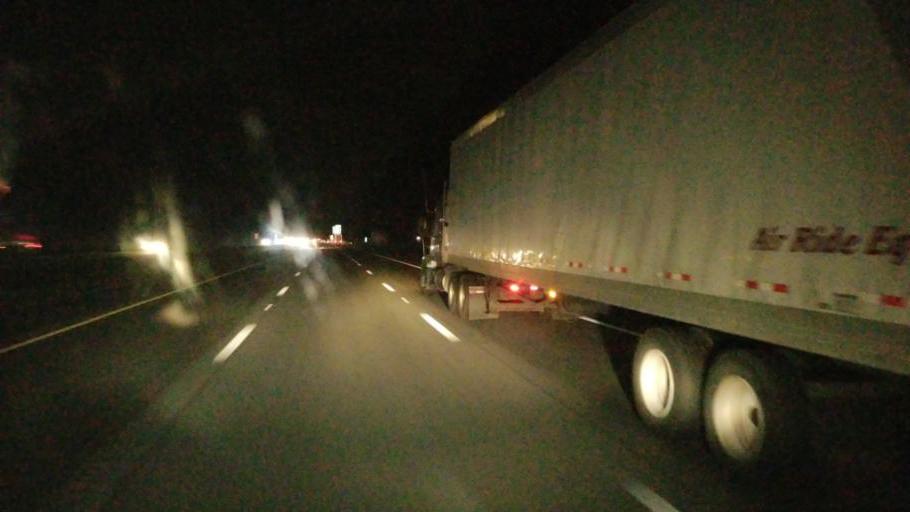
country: US
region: Ohio
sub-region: Richland County
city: Lincoln Heights
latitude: 40.7505
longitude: -82.4430
